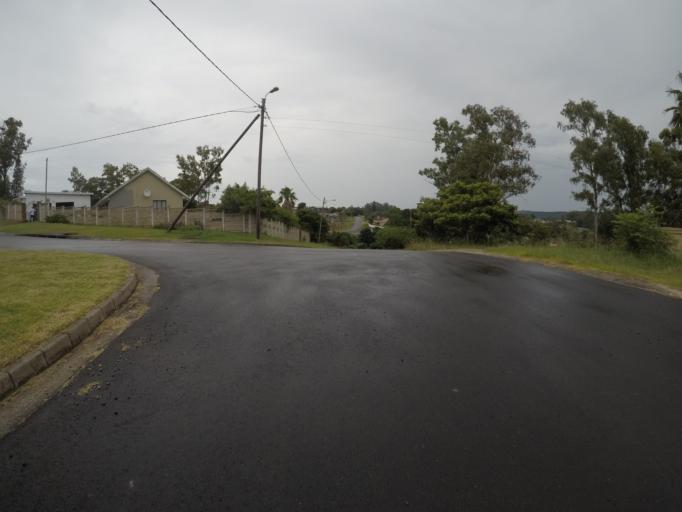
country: ZA
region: Eastern Cape
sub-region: Buffalo City Metropolitan Municipality
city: East London
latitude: -32.9636
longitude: 27.8489
